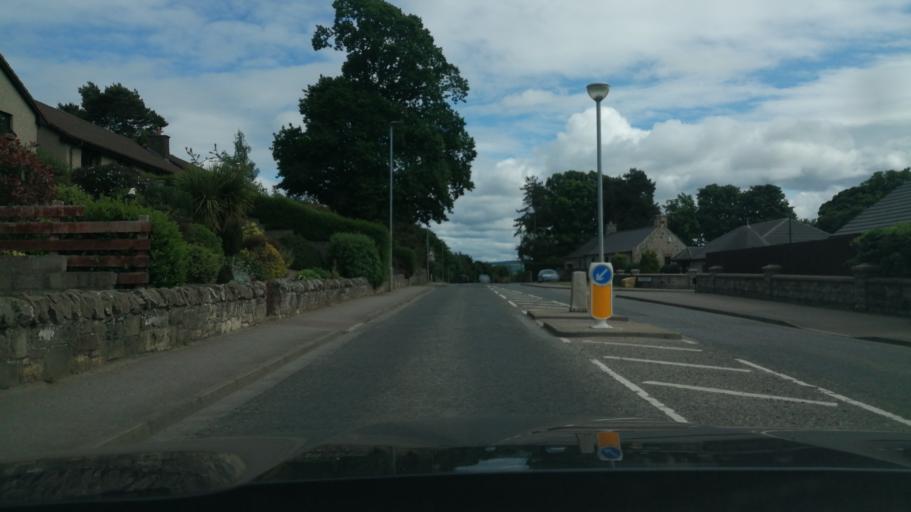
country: GB
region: Scotland
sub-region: Moray
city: Elgin
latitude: 57.6571
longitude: -3.3037
